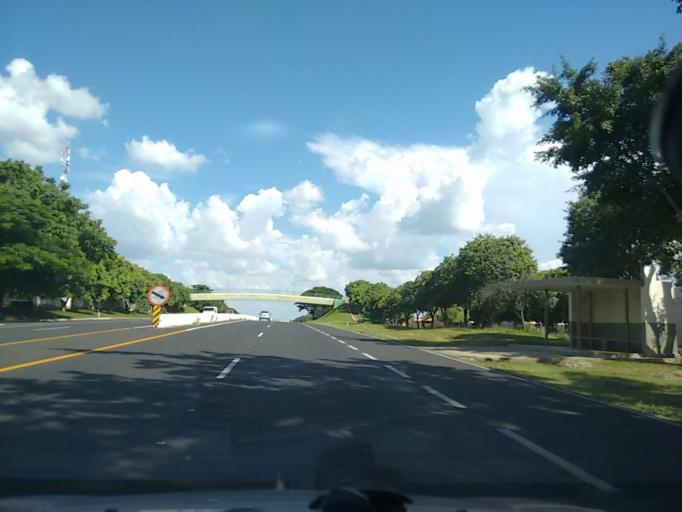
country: BR
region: Sao Paulo
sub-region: Pompeia
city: Pompeia
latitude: -22.1557
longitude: -50.0925
